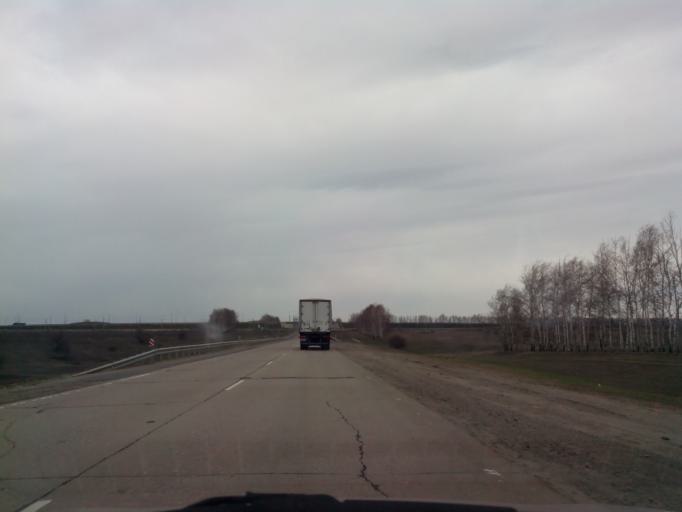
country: RU
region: Tambov
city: Pokrovo-Prigorodnoye
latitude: 52.6546
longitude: 41.3403
